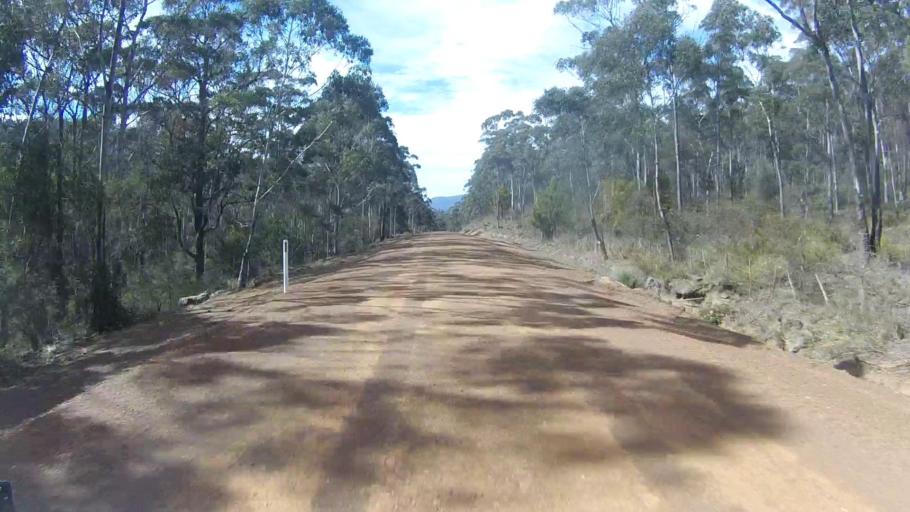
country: AU
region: Tasmania
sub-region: Sorell
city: Sorell
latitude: -42.6181
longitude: 147.9010
